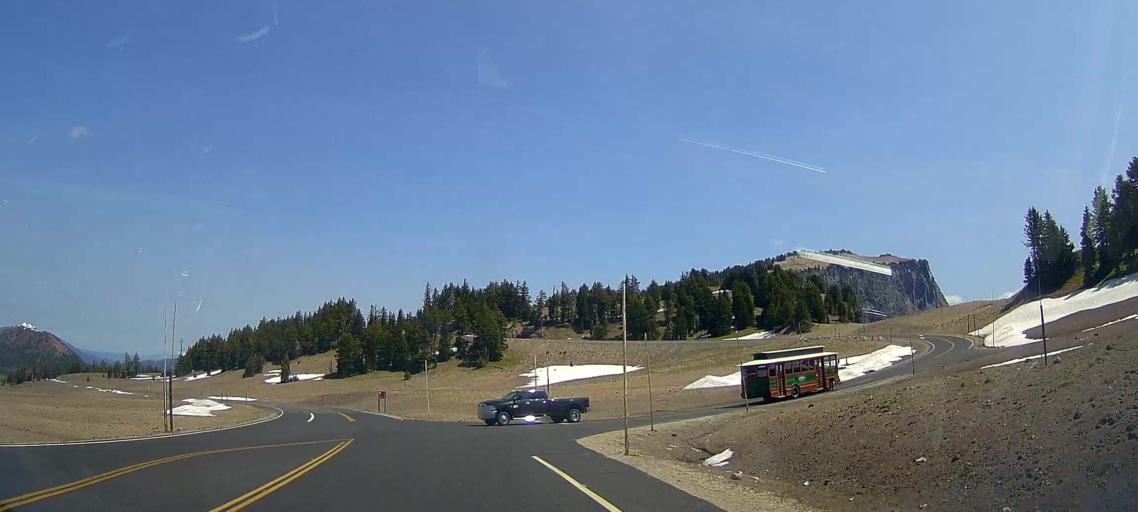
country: US
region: Oregon
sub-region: Jackson County
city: Shady Cove
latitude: 42.9652
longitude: -122.1533
